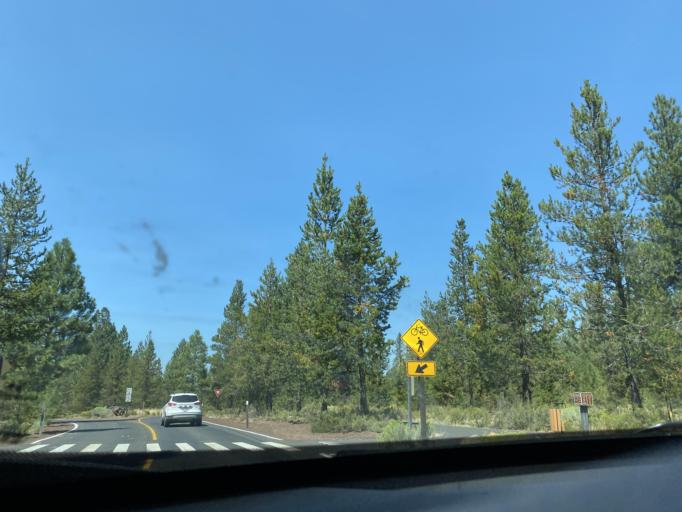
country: US
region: Oregon
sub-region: Deschutes County
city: Sunriver
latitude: 43.8899
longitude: -121.4371
